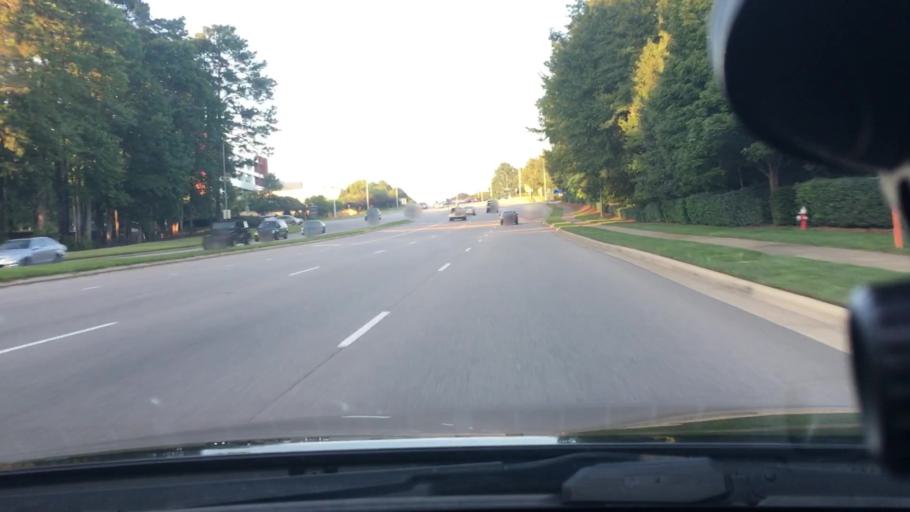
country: US
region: North Carolina
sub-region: Wake County
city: Cary
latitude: 35.7377
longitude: -78.7838
